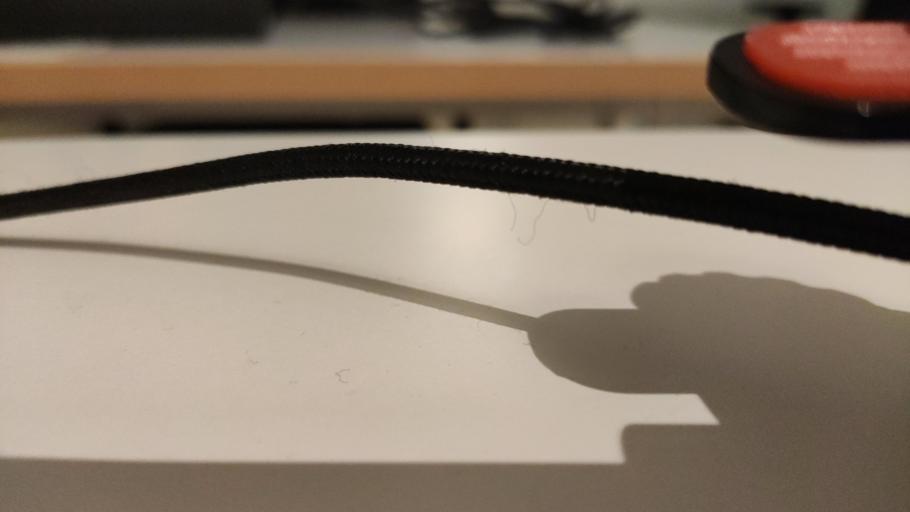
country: RU
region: Moskovskaya
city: Gorshkovo
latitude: 56.3735
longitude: 37.3926
